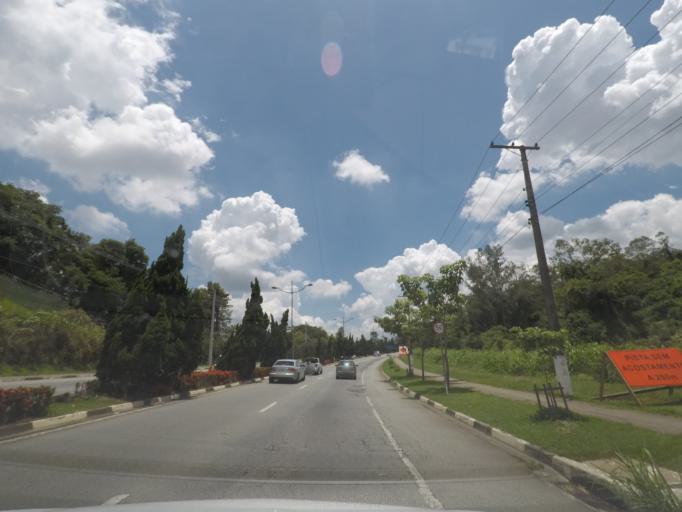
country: BR
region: Sao Paulo
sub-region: Vinhedo
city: Vinhedo
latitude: -23.0499
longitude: -46.9862
